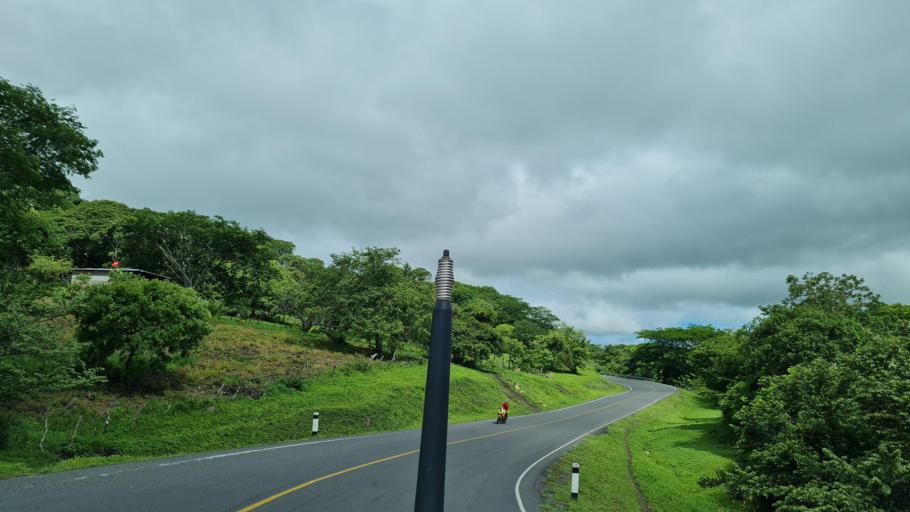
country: NI
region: Matagalpa
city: Terrabona
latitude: 12.5914
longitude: -85.9178
